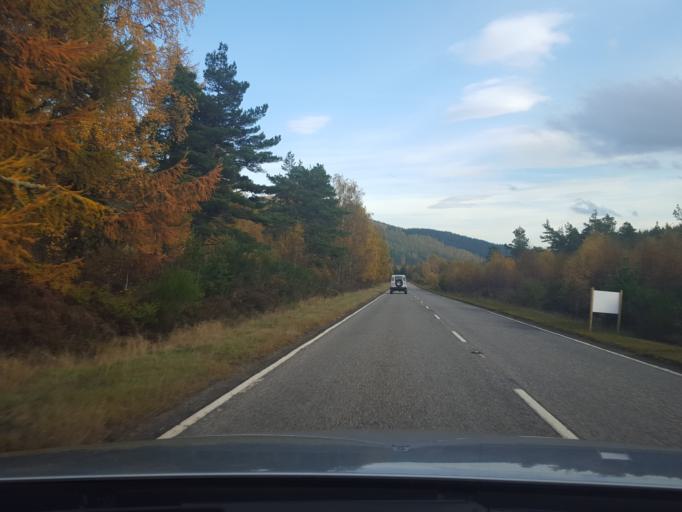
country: GB
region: Scotland
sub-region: Highland
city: Spean Bridge
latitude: 57.1967
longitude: -4.7373
